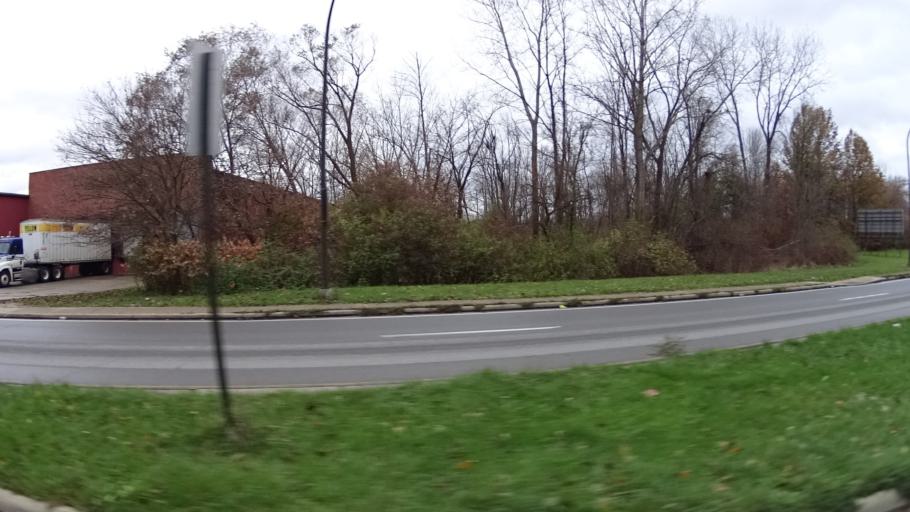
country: US
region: Ohio
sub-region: Lorain County
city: Elyria
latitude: 41.3576
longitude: -82.1174
